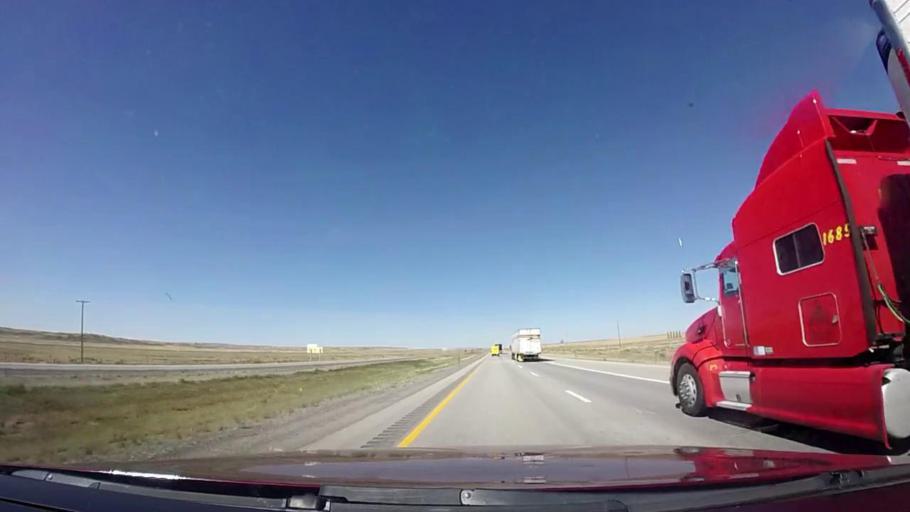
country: US
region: Wyoming
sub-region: Carbon County
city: Rawlins
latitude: 41.6647
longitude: -108.0381
